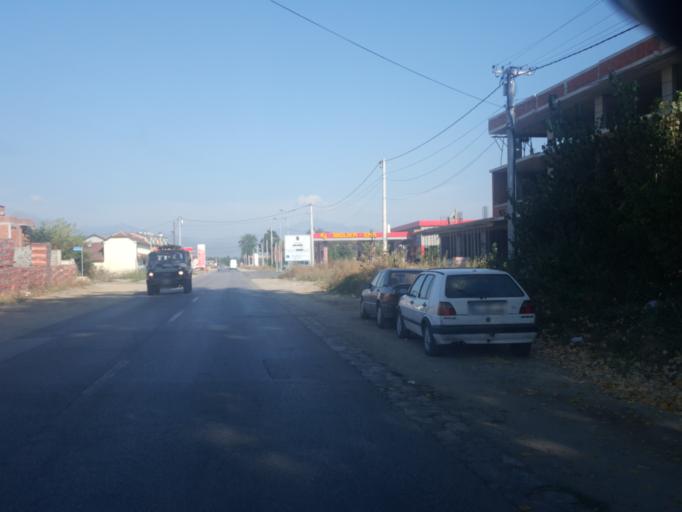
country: XK
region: Gjakova
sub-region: Komuna e Gjakoves
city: Gjakove
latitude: 42.4082
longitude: 20.4064
